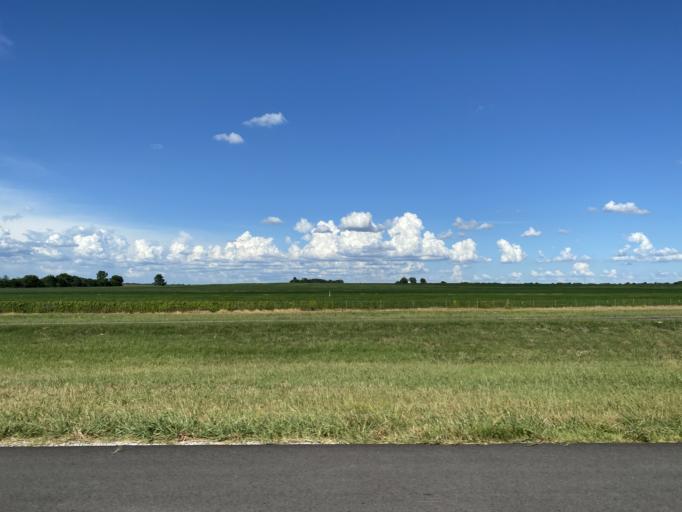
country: US
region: Alabama
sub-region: Limestone County
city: Athens
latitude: 34.7339
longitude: -86.9371
